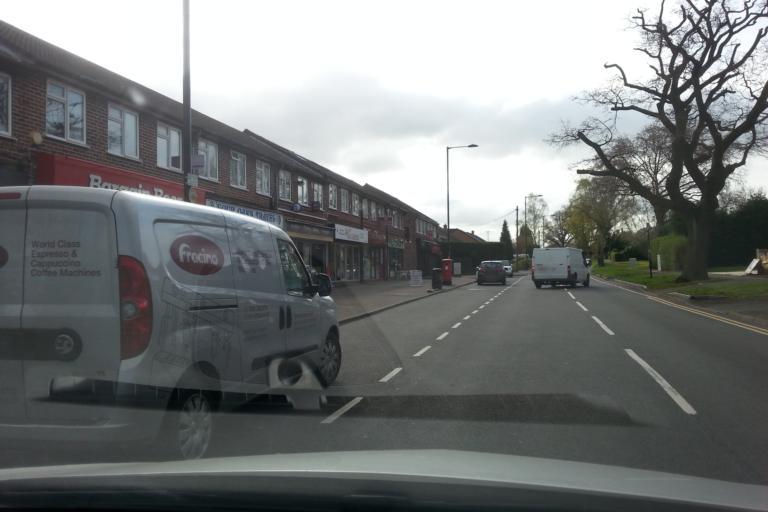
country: GB
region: England
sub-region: Staffordshire
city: Shenstone
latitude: 52.5991
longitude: -1.8481
